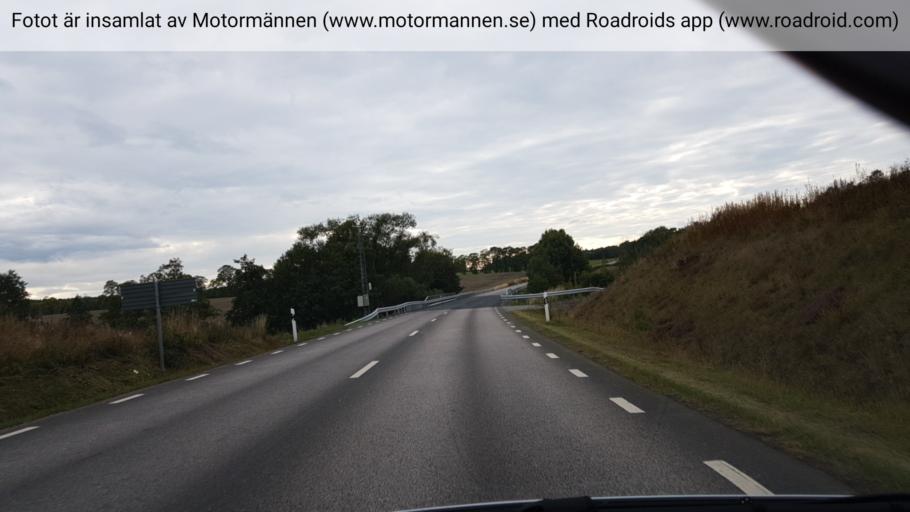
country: SE
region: Vaestra Goetaland
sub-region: Tibro Kommun
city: Tibro
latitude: 58.3458
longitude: 14.1246
